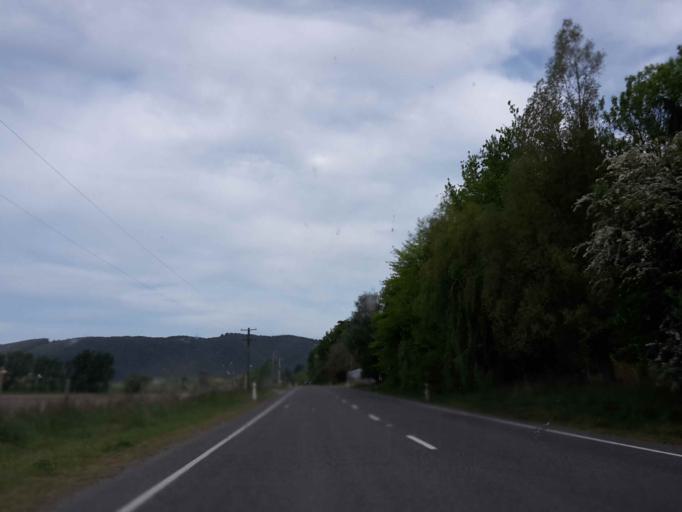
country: NZ
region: Canterbury
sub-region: Timaru District
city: Pleasant Point
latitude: -44.1117
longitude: 171.0142
